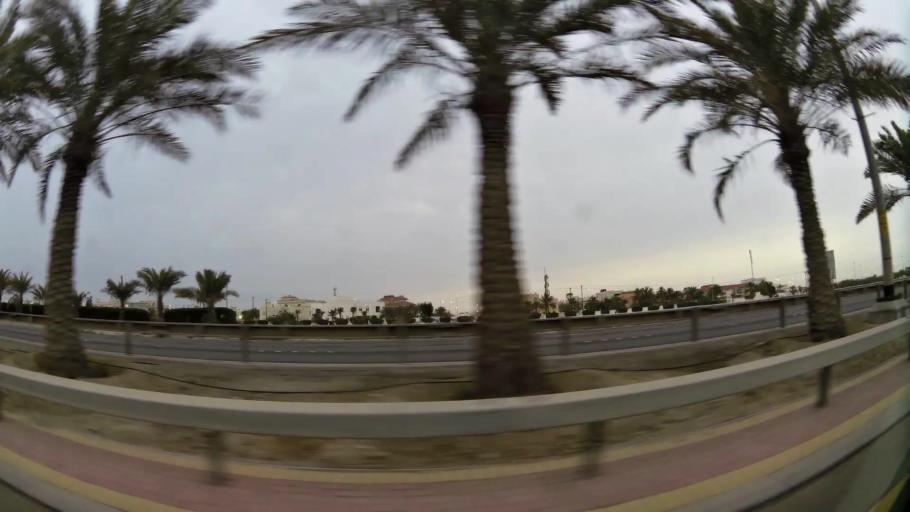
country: BH
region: Northern
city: Madinat `Isa
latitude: 26.1550
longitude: 50.5365
